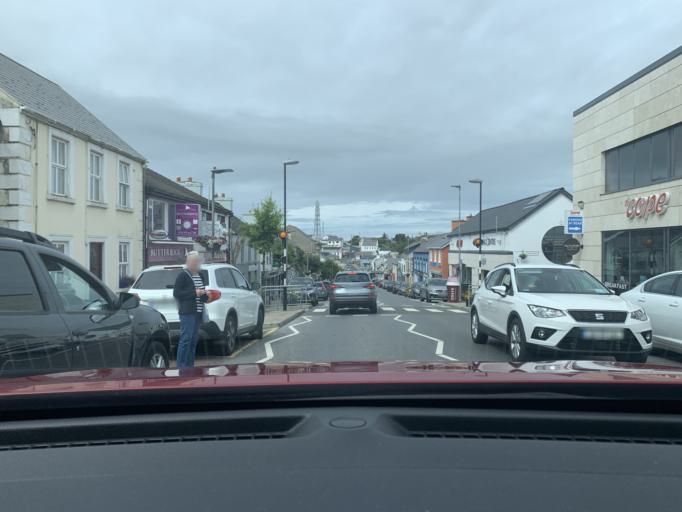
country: IE
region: Ulster
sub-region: County Donegal
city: Dungloe
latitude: 54.9486
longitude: -8.3601
